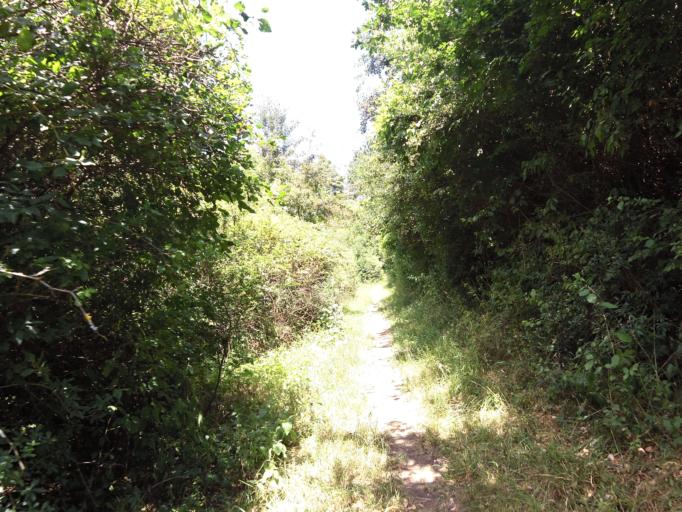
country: DE
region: Bavaria
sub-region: Regierungsbezirk Unterfranken
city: Hochberg
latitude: 49.7799
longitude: 9.8974
